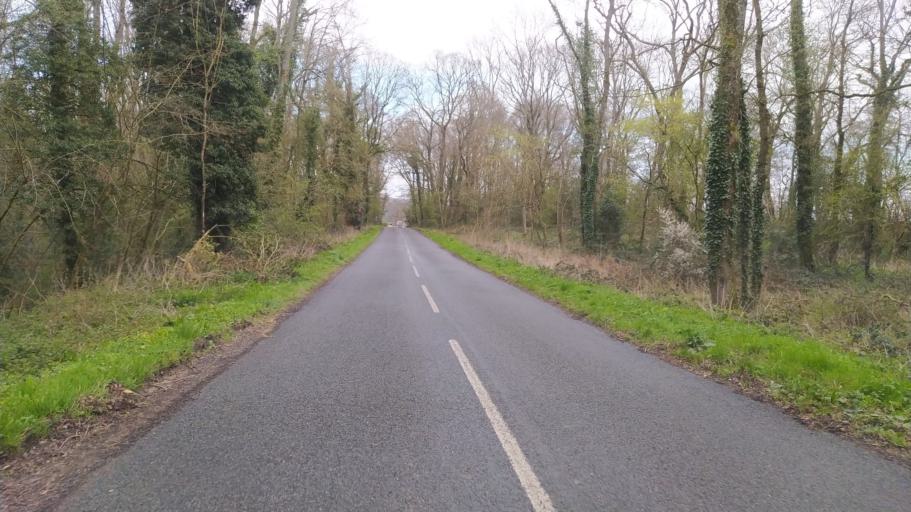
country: GB
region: England
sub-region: West Sussex
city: Petworth
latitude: 51.0252
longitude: -0.5958
